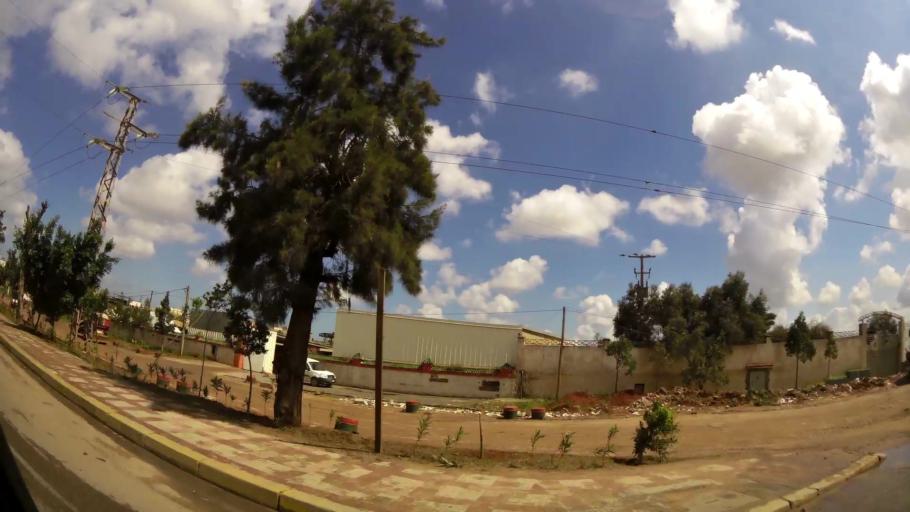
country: MA
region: Grand Casablanca
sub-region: Casablanca
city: Casablanca
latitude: 33.5296
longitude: -7.5675
